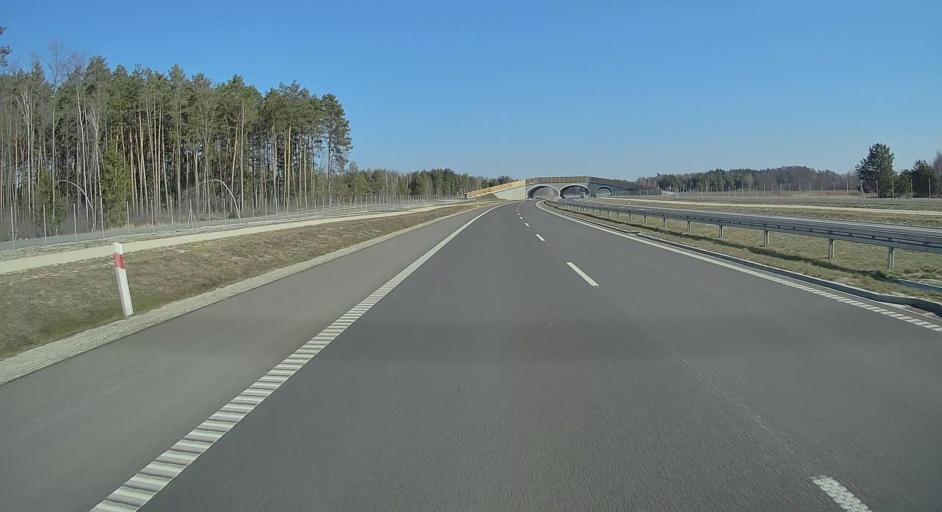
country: PL
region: Subcarpathian Voivodeship
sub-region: Powiat nizanski
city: Jarocin
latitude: 50.5930
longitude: 22.2597
